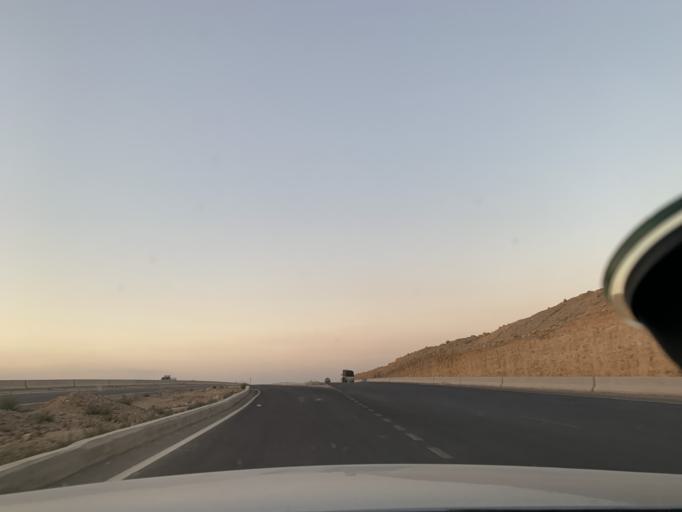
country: EG
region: Muhafazat al Qahirah
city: Halwan
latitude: 29.9517
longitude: 31.5394
